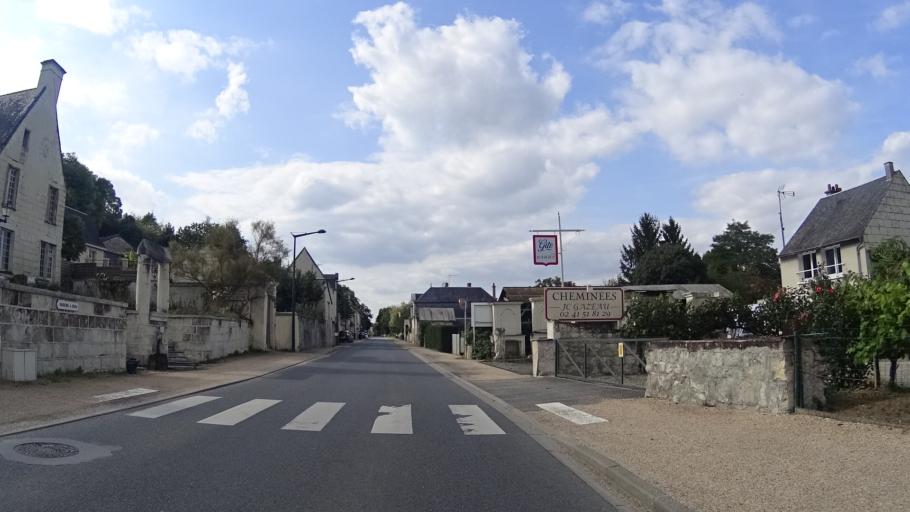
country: FR
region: Pays de la Loire
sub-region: Departement de Maine-et-Loire
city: Villebernier
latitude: 47.2415
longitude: -0.0249
